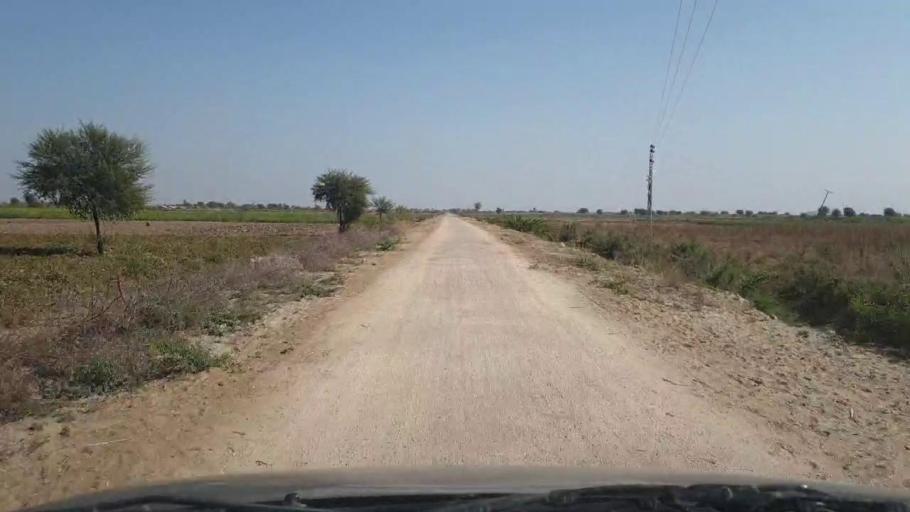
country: PK
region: Sindh
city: Samaro
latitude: 25.1992
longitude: 69.2913
